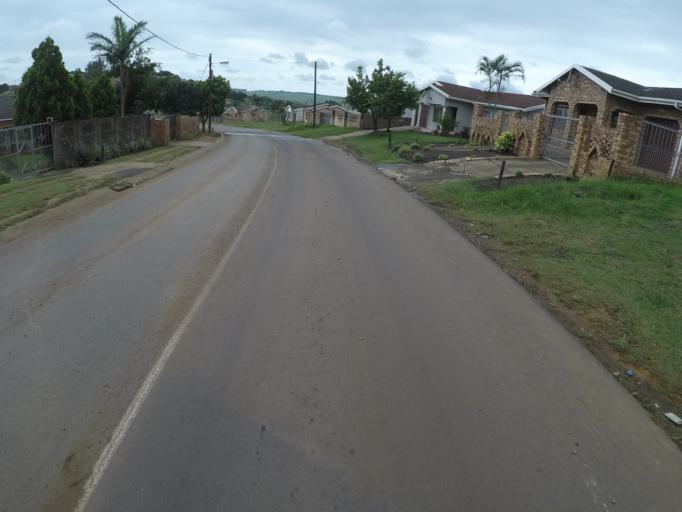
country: ZA
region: KwaZulu-Natal
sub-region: uThungulu District Municipality
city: Empangeni
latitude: -28.7854
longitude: 31.8513
